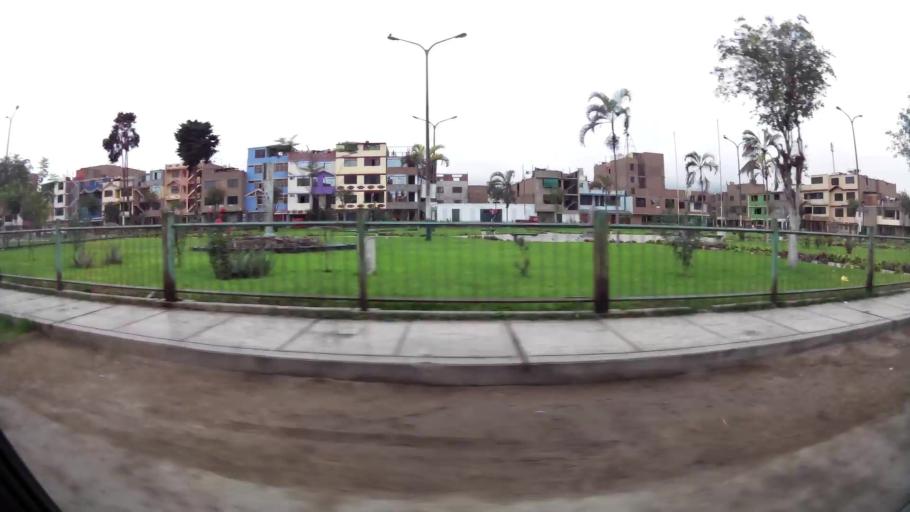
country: PE
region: Lima
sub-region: Lima
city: Independencia
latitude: -11.9734
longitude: -77.0714
